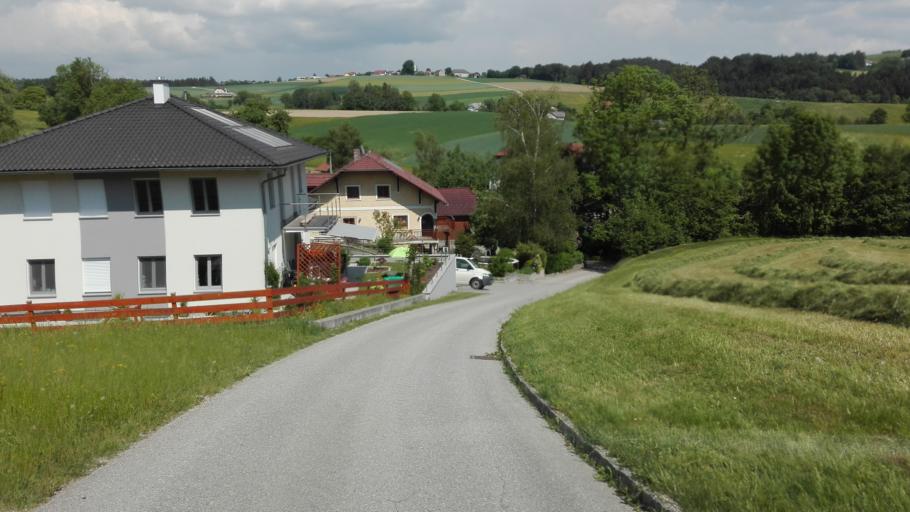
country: AT
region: Upper Austria
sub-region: Politischer Bezirk Rohrbach
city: Atzesberg
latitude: 48.4058
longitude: 13.8959
